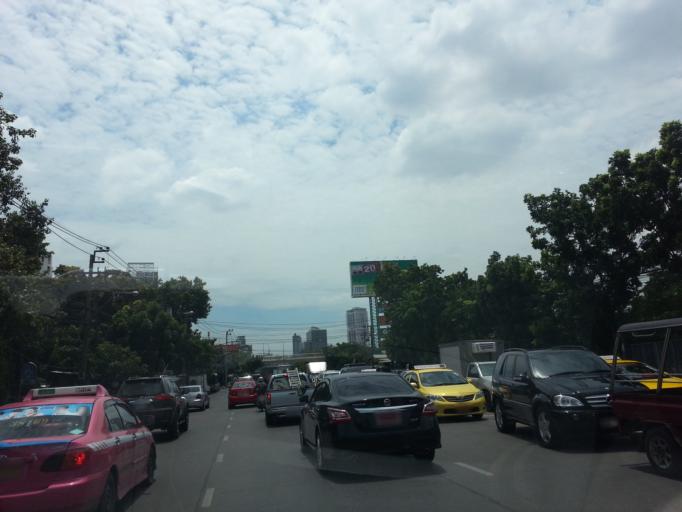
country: TH
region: Bangkok
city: Khlong Toei
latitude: 13.7161
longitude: 100.5659
